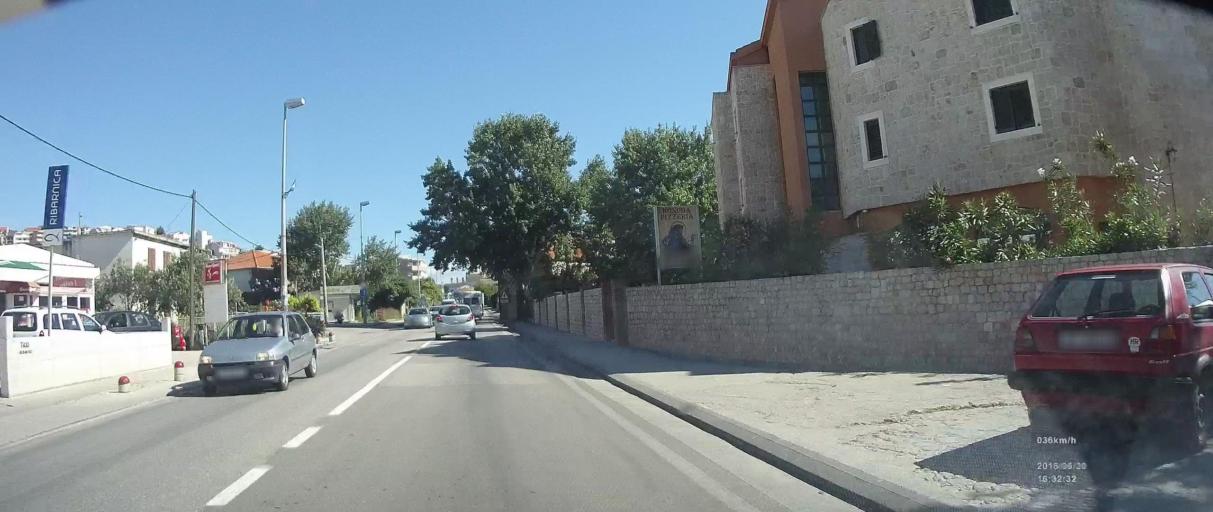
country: HR
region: Splitsko-Dalmatinska
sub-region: Grad Split
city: Stobrec
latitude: 43.5015
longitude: 16.5349
